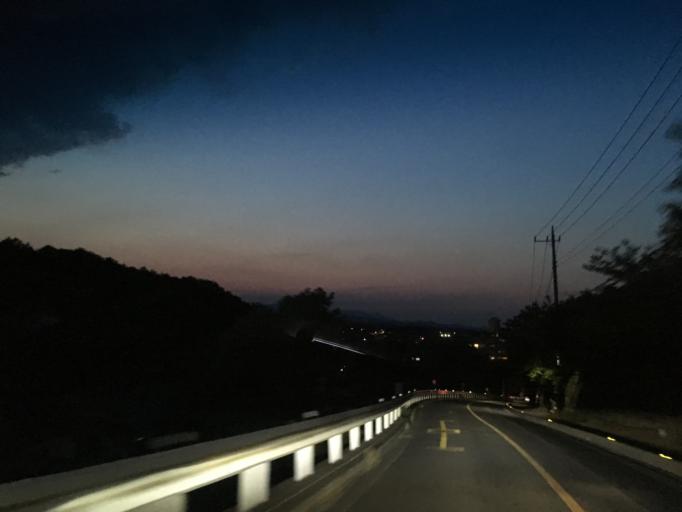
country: JP
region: Saitama
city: Sayama
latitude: 35.8389
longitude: 139.3781
